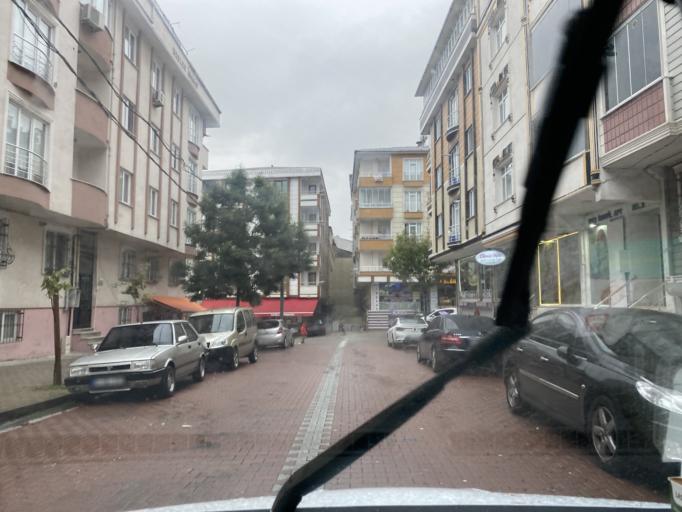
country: TR
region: Istanbul
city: Esenyurt
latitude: 41.0189
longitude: 28.6624
